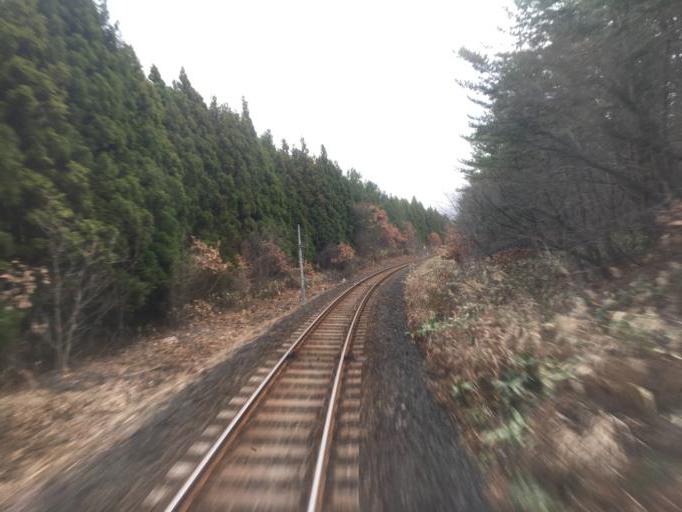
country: JP
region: Aomori
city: Mutsu
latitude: 41.0106
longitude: 141.2378
